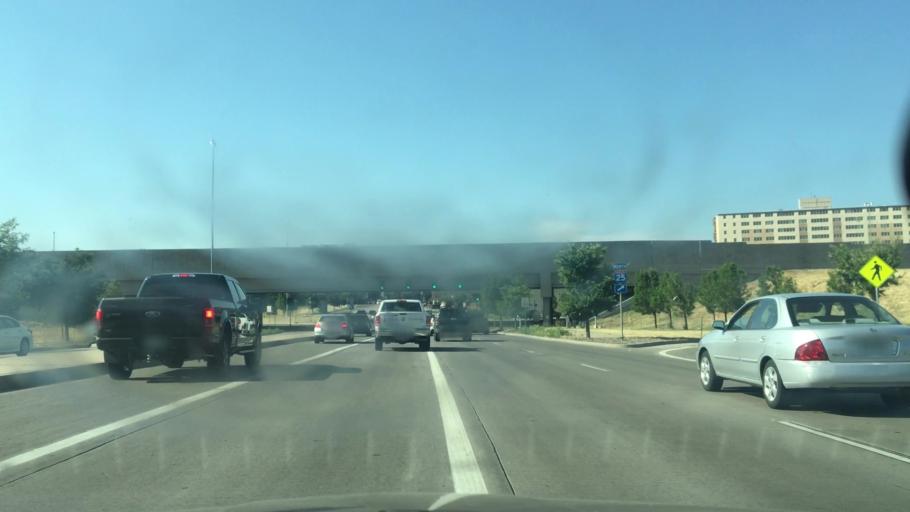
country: US
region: Colorado
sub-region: Arapahoe County
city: Glendale
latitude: 39.6860
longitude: -104.9595
